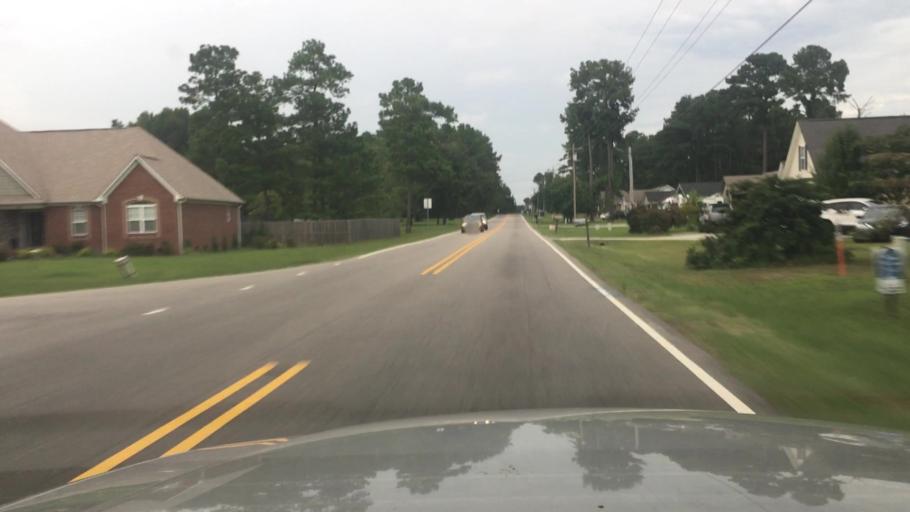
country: US
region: North Carolina
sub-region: Hoke County
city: Rockfish
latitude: 34.9583
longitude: -79.0533
